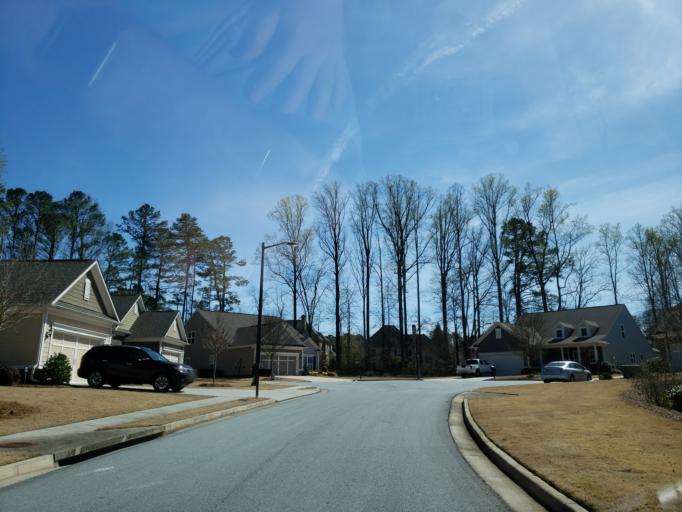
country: US
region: Georgia
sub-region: Cobb County
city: Marietta
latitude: 34.0210
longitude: -84.5079
